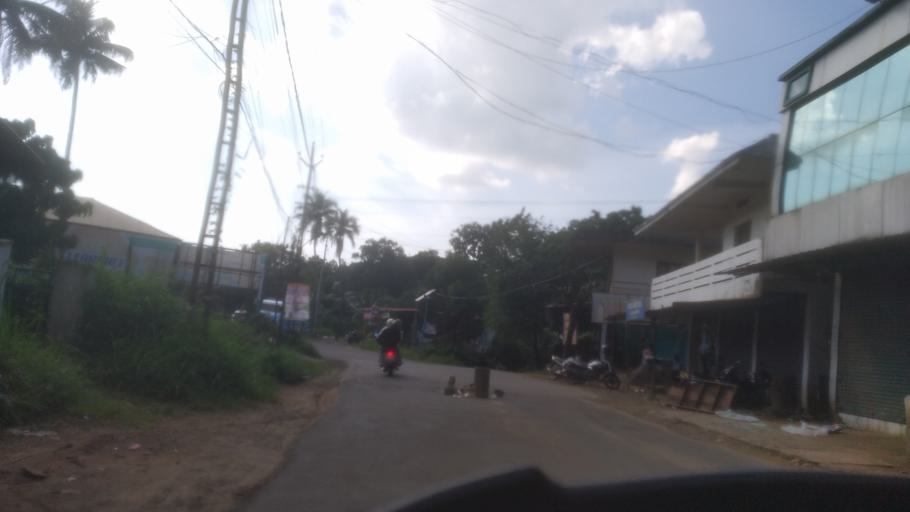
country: IN
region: Kerala
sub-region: Ernakulam
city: Muvattupula
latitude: 9.9976
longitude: 76.6013
